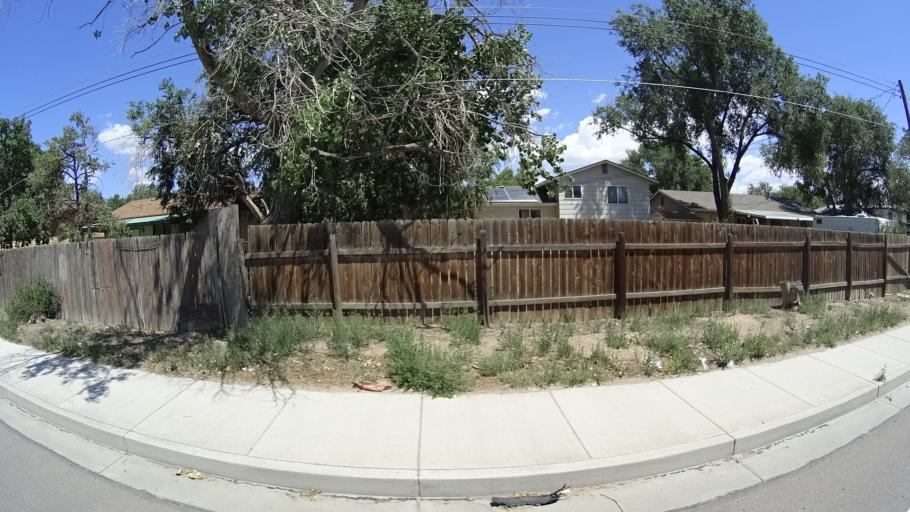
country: US
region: Colorado
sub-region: El Paso County
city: Stratmoor
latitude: 38.7935
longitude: -104.7667
